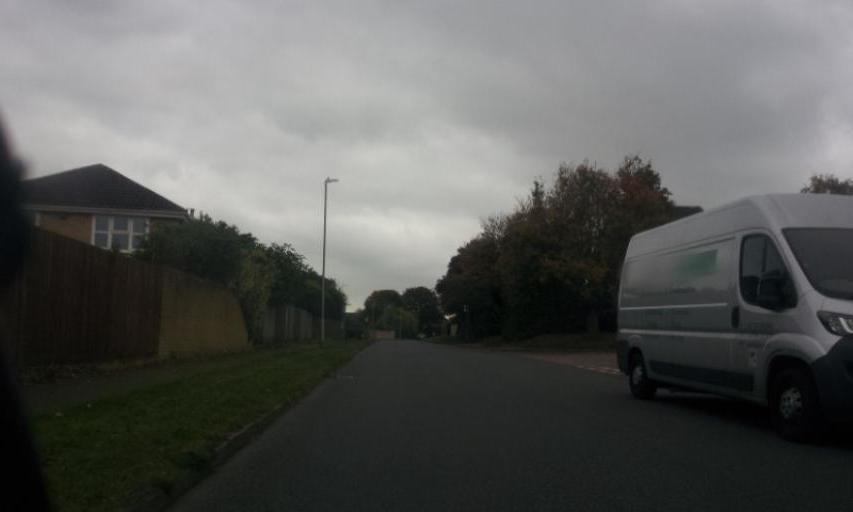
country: GB
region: England
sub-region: Kent
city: Larkfield
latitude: 51.3087
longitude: 0.4401
